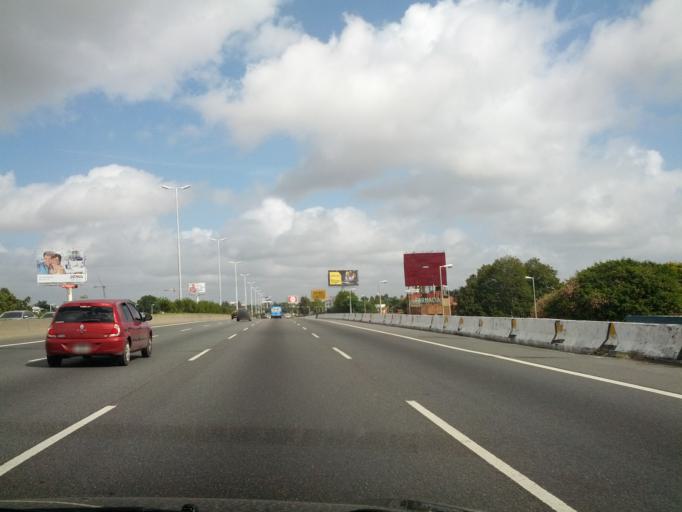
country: AR
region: Buenos Aires
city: Caseros
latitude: -34.6311
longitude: -58.5749
